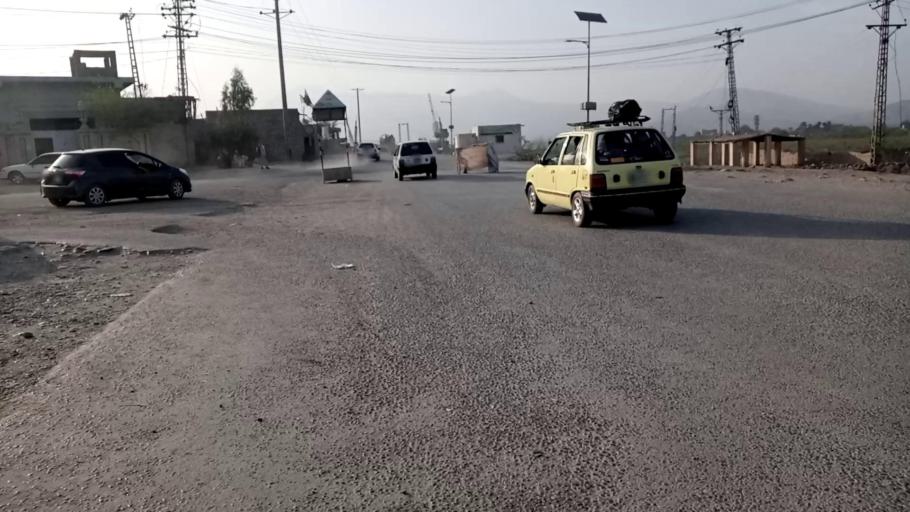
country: PK
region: Khyber Pakhtunkhwa
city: Peshawar
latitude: 33.9981
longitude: 71.4032
